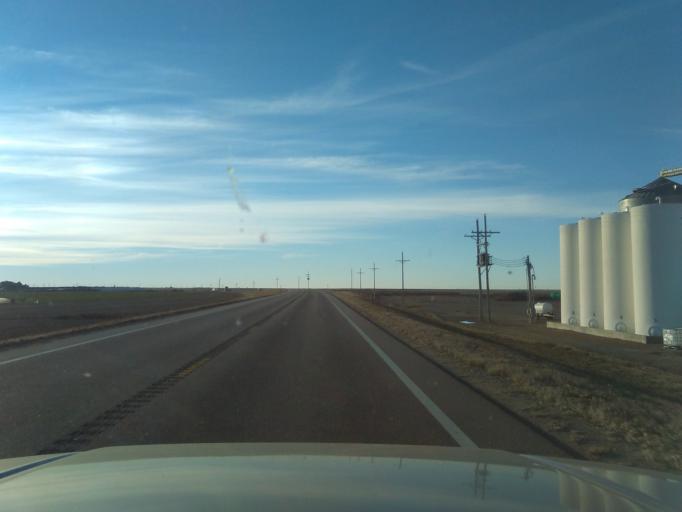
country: US
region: Kansas
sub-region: Thomas County
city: Colby
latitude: 39.4480
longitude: -100.8169
